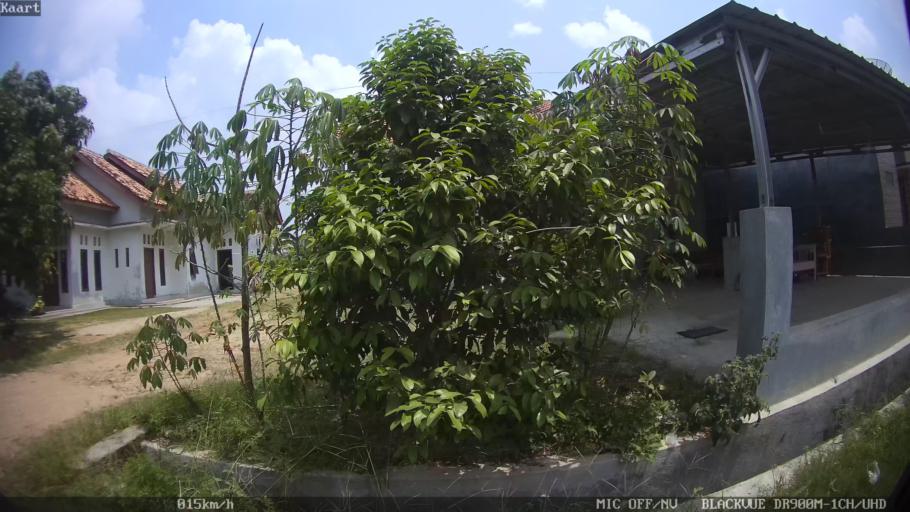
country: ID
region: Lampung
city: Pringsewu
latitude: -5.3559
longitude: 104.9890
